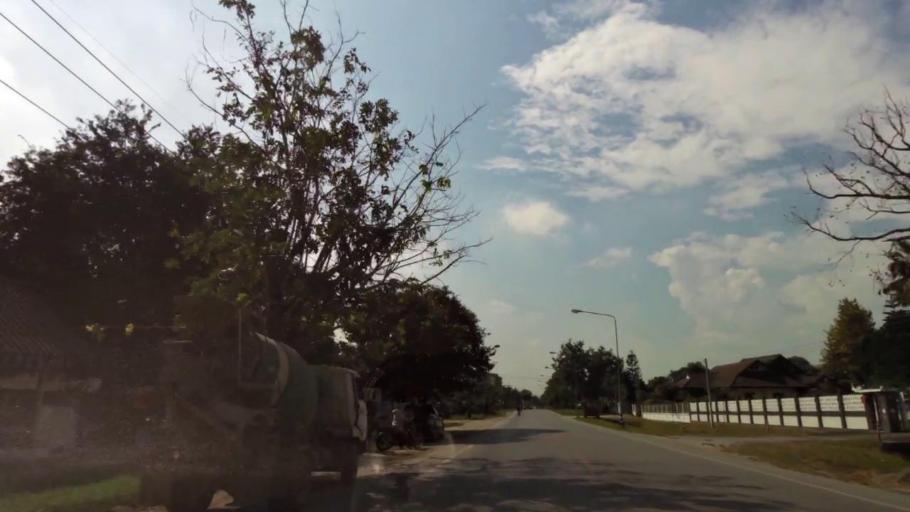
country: TH
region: Chiang Rai
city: Chiang Rai
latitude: 19.8598
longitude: 99.7644
